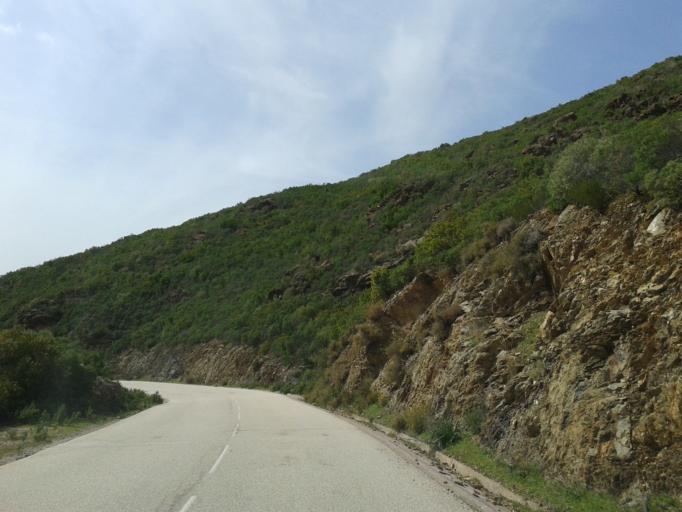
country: FR
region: Corsica
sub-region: Departement de la Haute-Corse
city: Saint-Florent
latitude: 42.6616
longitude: 9.1302
